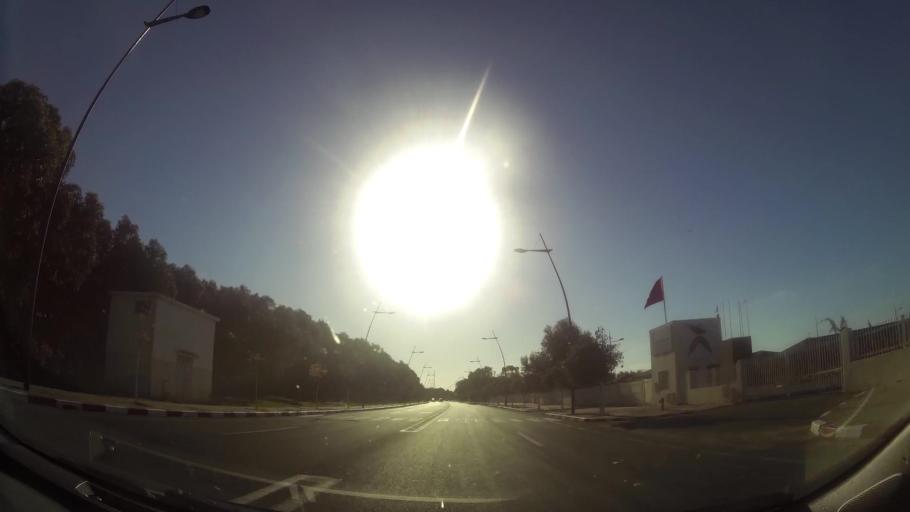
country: MA
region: Oriental
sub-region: Berkane-Taourirt
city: Madagh
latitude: 35.0898
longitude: -2.2456
